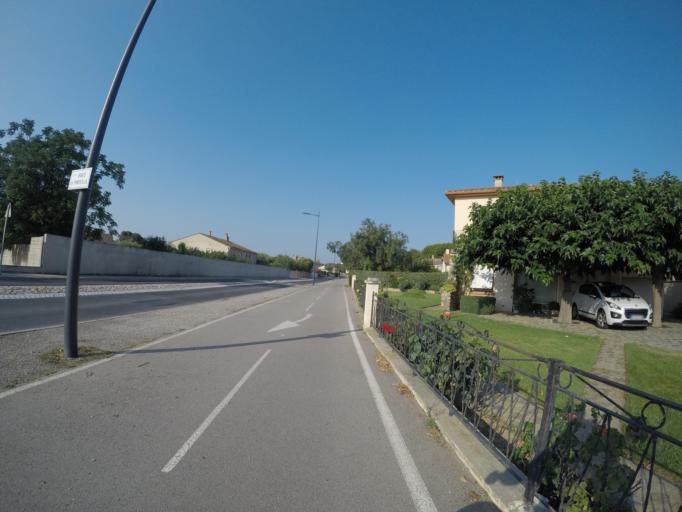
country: FR
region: Languedoc-Roussillon
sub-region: Departement des Pyrenees-Orientales
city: Canohes
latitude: 42.6512
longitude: 2.8301
